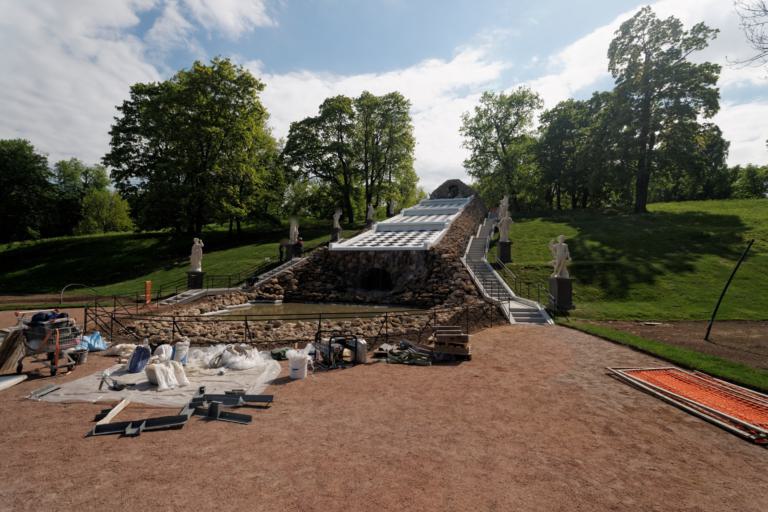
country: RU
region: St.-Petersburg
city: Peterhof
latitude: 59.8836
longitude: 29.9166
